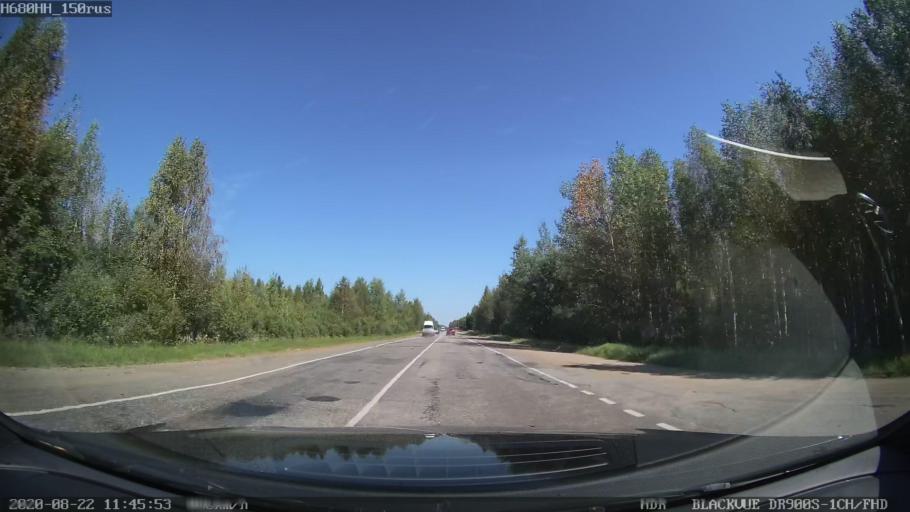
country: RU
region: Tverskaya
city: Sakharovo
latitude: 57.0358
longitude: 36.0687
